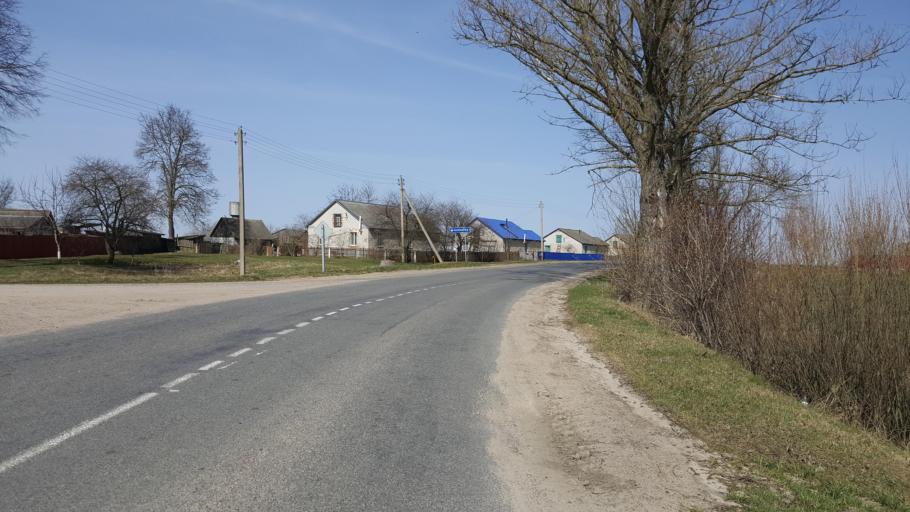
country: BY
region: Brest
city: Kamyanyets
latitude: 52.4315
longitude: 23.7499
